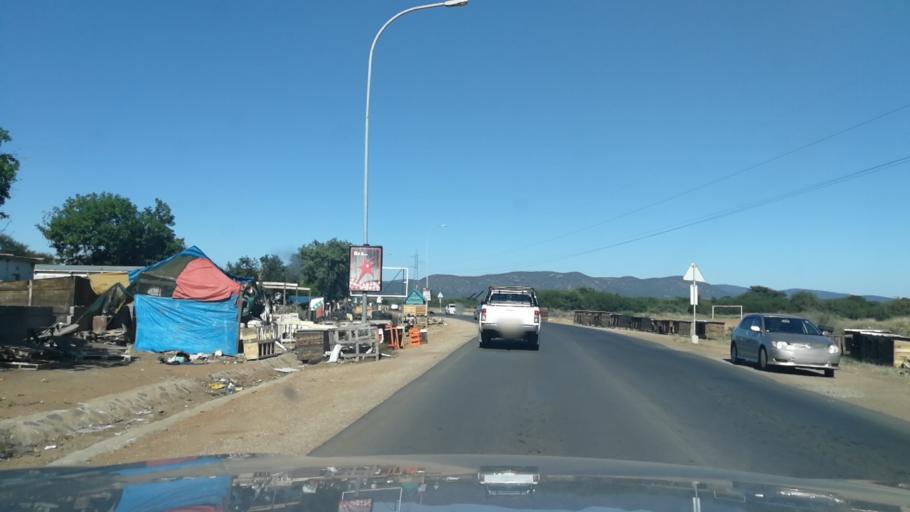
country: BW
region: South East
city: Gaborone
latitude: -24.6933
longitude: 25.8907
